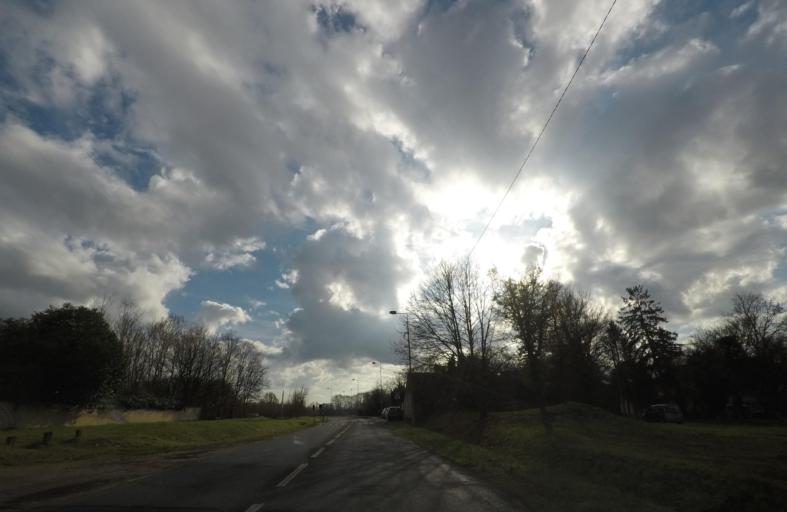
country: FR
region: Centre
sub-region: Departement du Cher
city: Bourges
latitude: 47.0517
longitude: 2.4065
